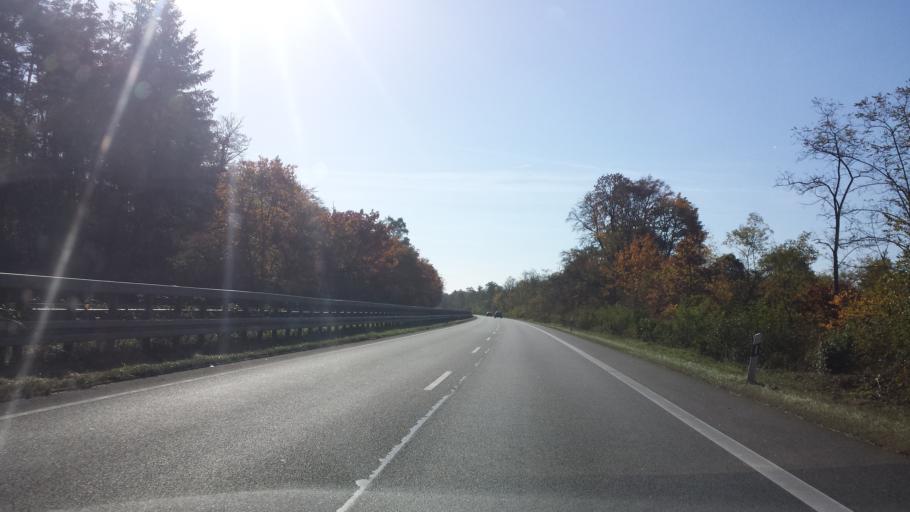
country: DE
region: Hesse
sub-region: Regierungsbezirk Darmstadt
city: Darmstadt
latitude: 49.8382
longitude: 8.6366
